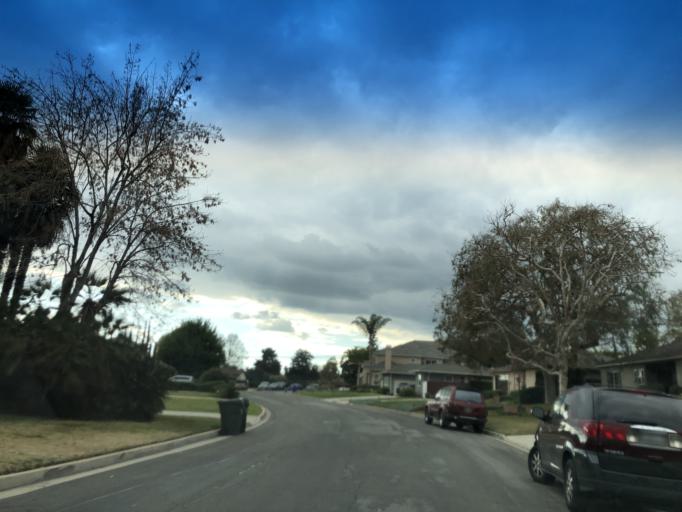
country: US
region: California
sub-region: Los Angeles County
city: San Marino
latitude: 34.1252
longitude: -118.0882
